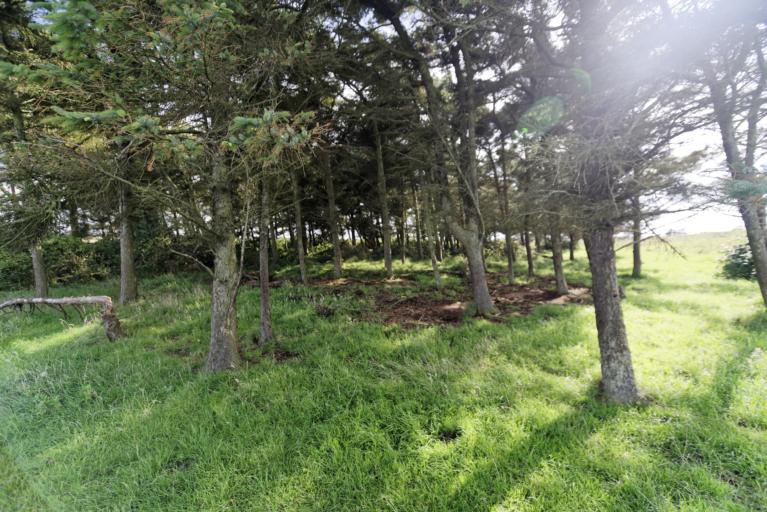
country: NL
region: North Holland
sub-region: Gemeente Texel
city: Den Burg
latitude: 53.1156
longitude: 4.7886
